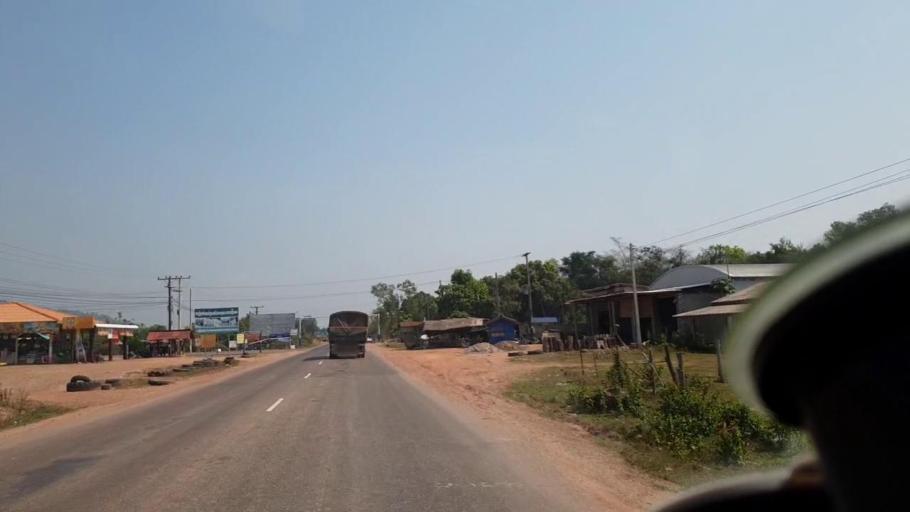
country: TH
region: Nong Khai
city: Rattanawapi
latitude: 18.1980
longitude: 103.0588
